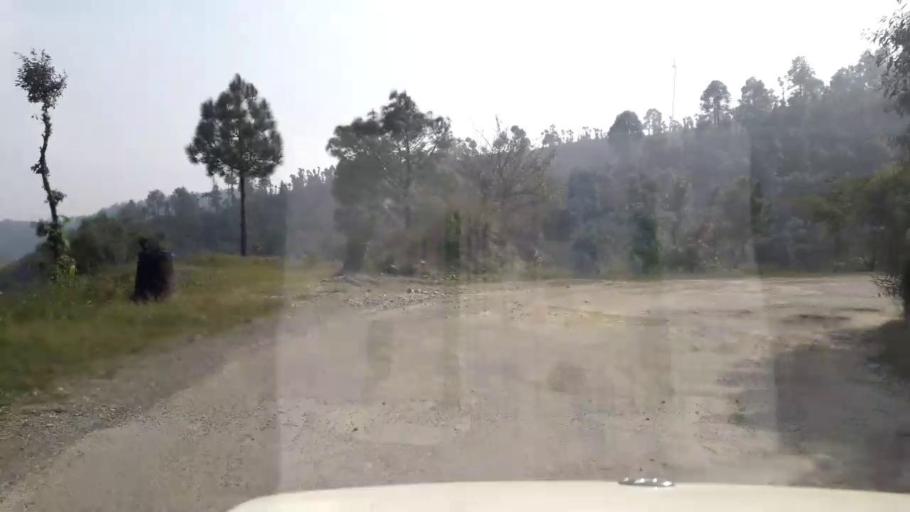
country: IN
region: Himachal Pradesh
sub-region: Shimla
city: Shimla
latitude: 31.0517
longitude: 77.1511
